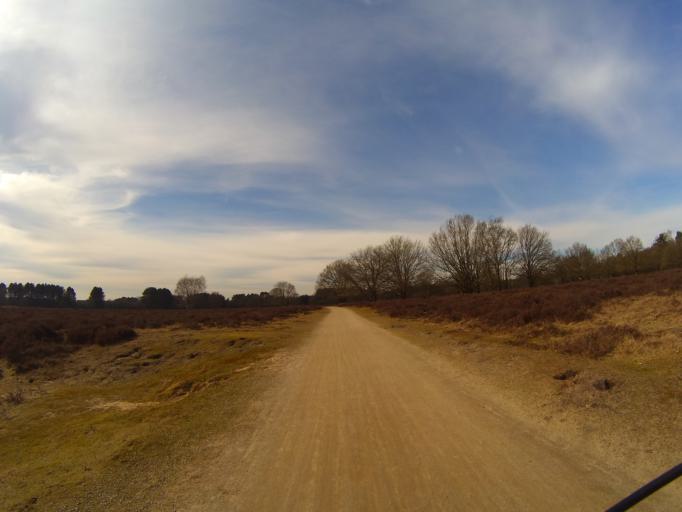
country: NL
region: North Holland
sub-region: Gemeente Laren
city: Laren
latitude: 52.2343
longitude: 5.2085
